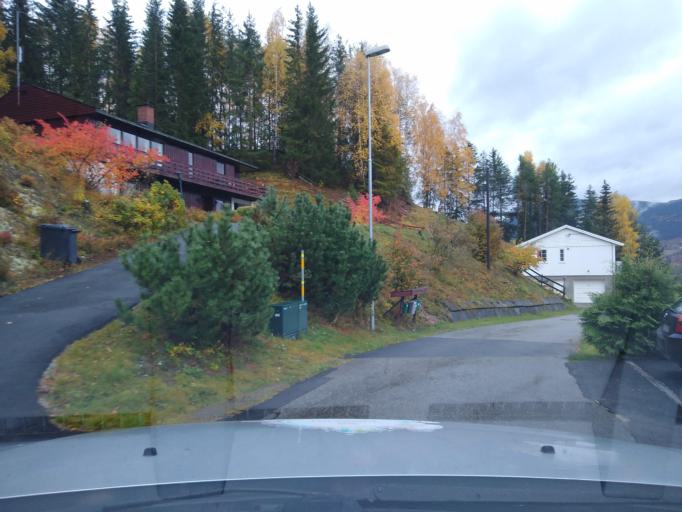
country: NO
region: Oppland
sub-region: Ringebu
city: Ringebu
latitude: 61.4576
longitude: 10.2013
